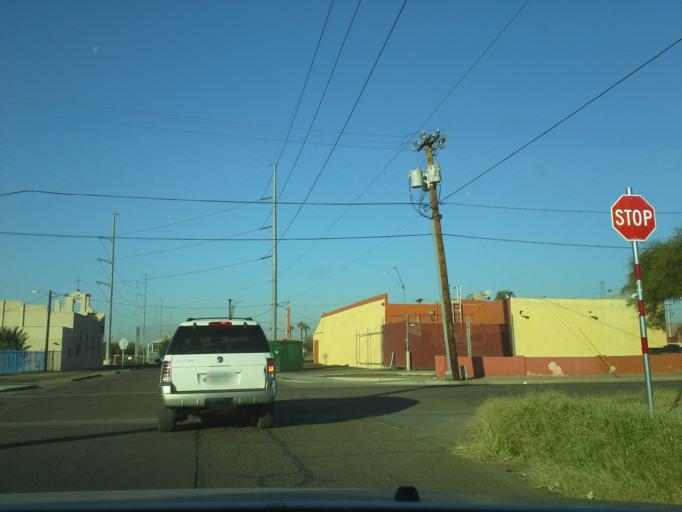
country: US
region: Arizona
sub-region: Maricopa County
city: Phoenix
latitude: 33.4401
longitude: -112.0813
